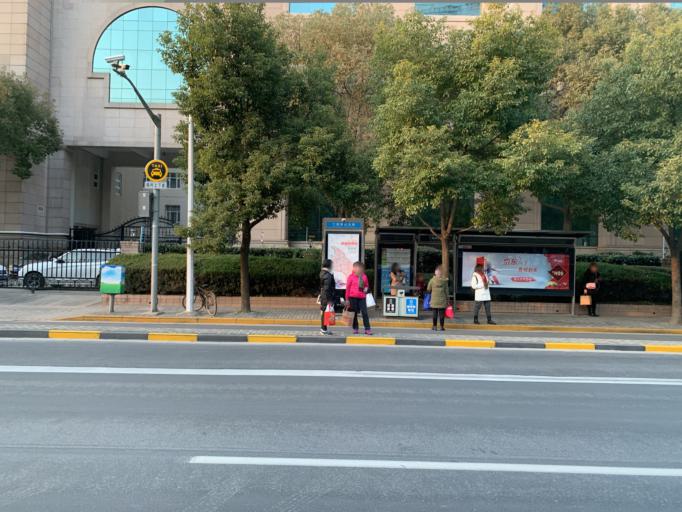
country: CN
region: Shanghai Shi
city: Huamu
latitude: 31.2273
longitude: 121.5442
